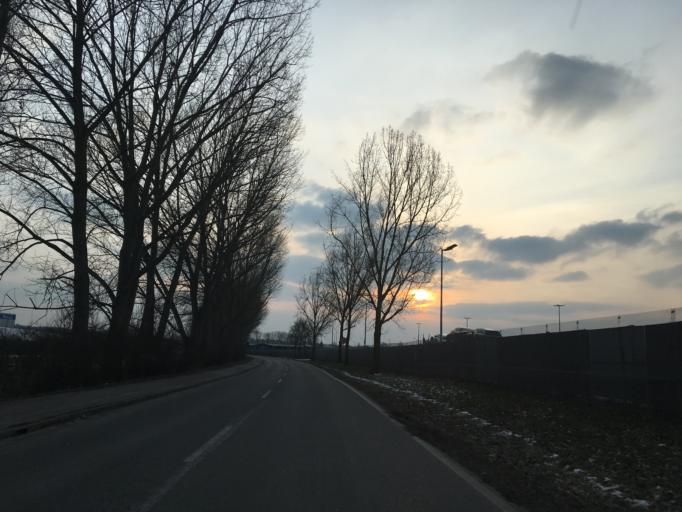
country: DE
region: Baden-Wuerttemberg
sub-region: Regierungsbezirk Stuttgart
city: Boeblingen
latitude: 48.6929
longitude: 8.9916
